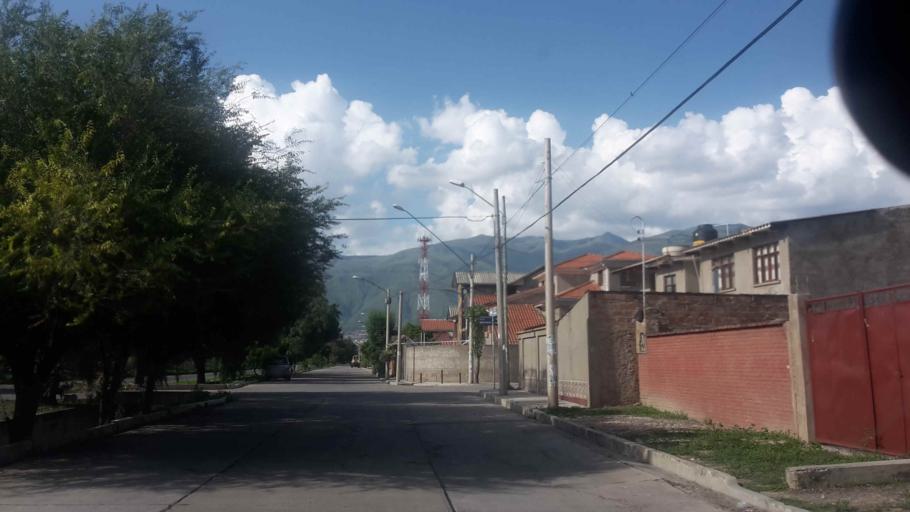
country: BO
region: Cochabamba
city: Cochabamba
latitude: -17.3845
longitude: -66.1963
